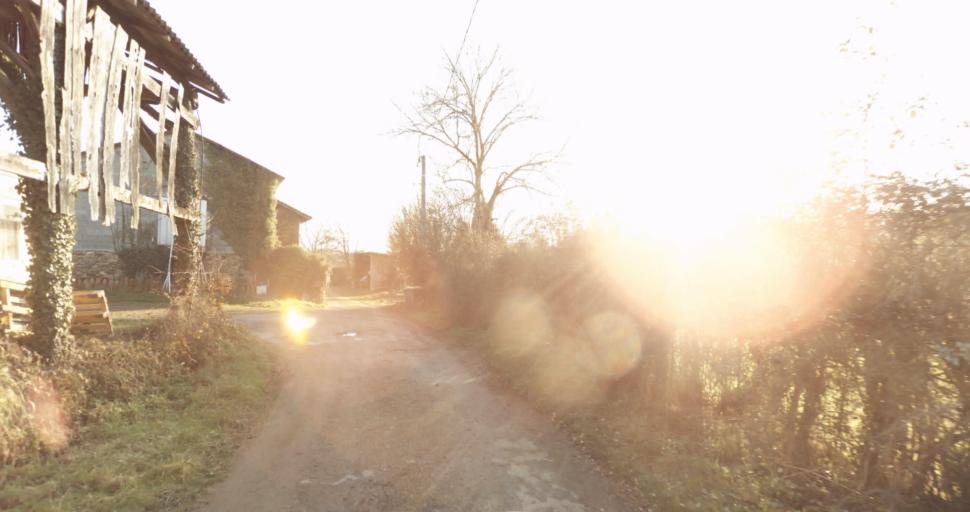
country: FR
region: Limousin
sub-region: Departement de la Haute-Vienne
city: Aixe-sur-Vienne
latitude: 45.7876
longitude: 1.1359
